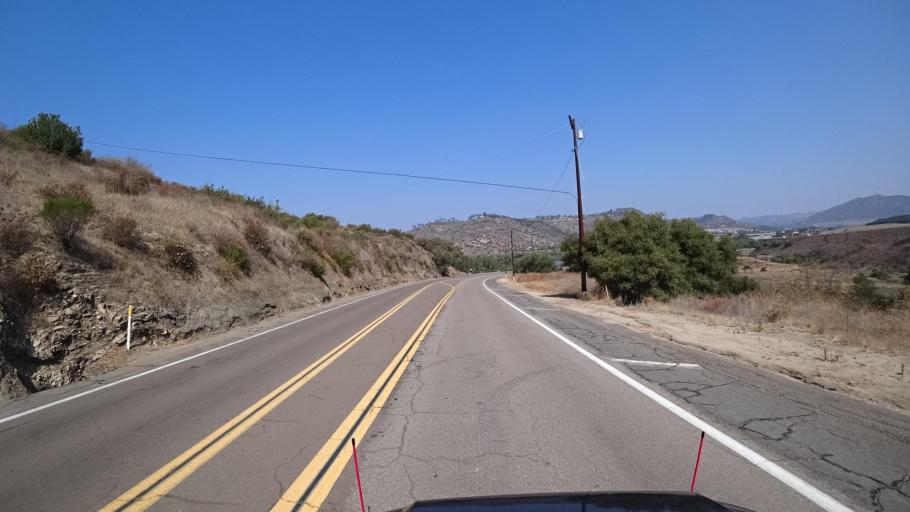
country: US
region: California
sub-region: San Diego County
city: Bonsall
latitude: 33.3165
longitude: -117.1580
